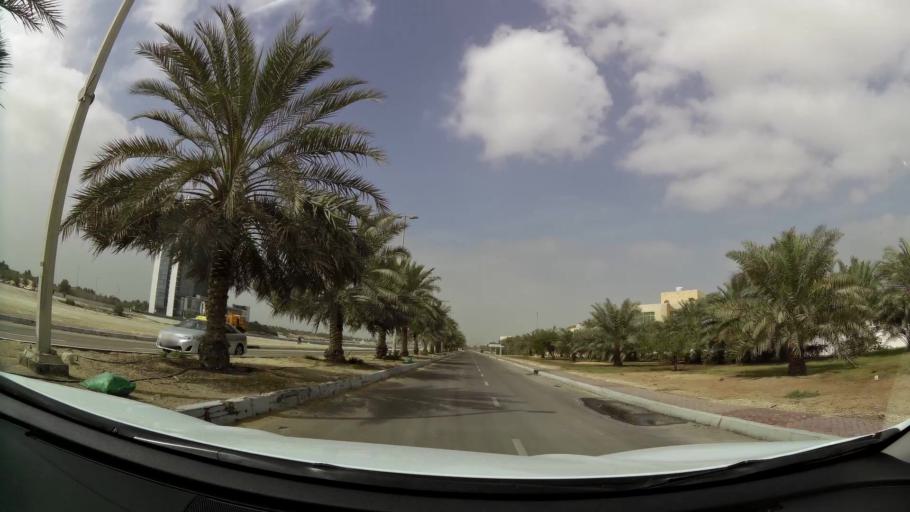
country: AE
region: Abu Dhabi
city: Abu Dhabi
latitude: 24.3969
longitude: 54.5212
